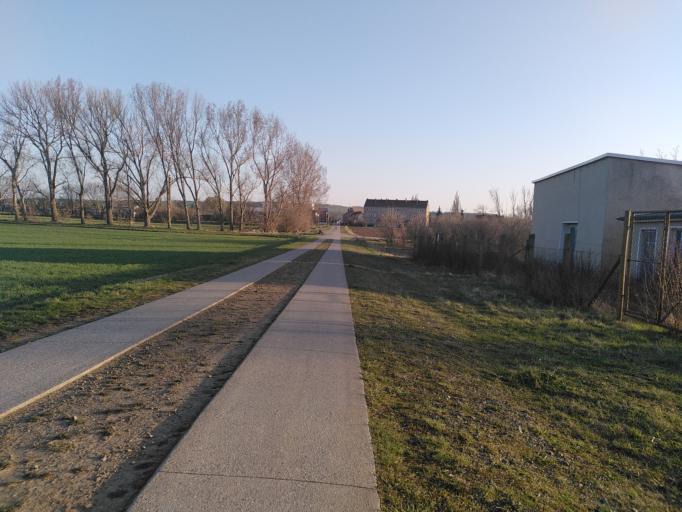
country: DE
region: Saxony-Anhalt
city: Ditfurt
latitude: 51.7928
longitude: 11.2046
